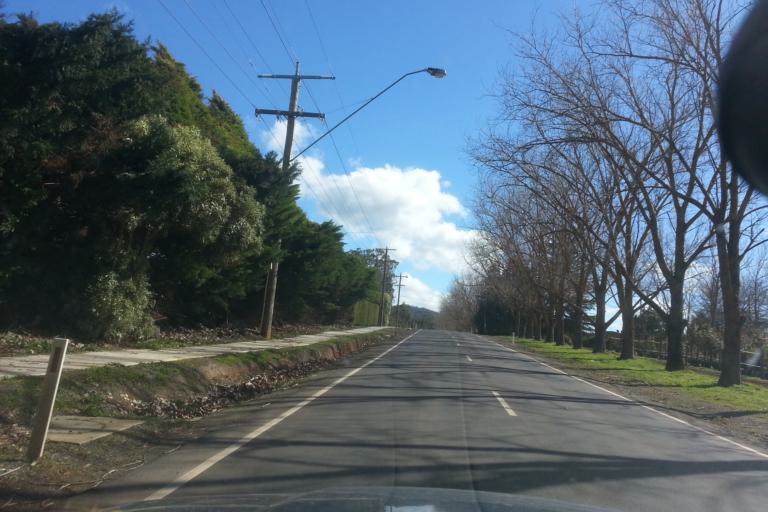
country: AU
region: Victoria
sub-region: Yarra Ranges
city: Monbulk
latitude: -37.8644
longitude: 145.4217
